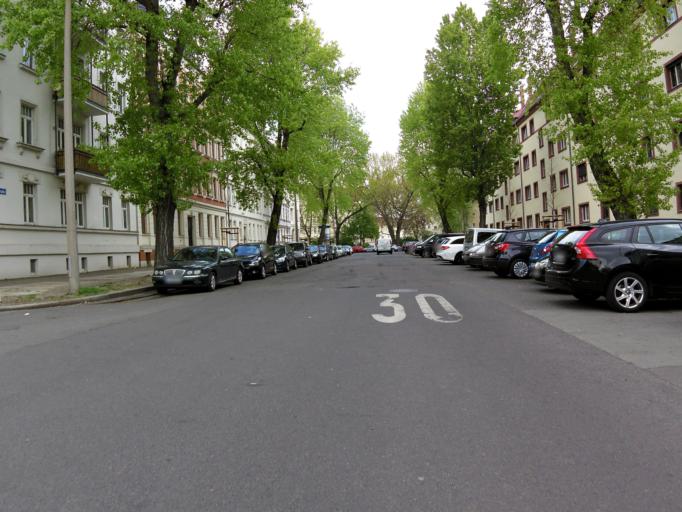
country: DE
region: Saxony
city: Leipzig
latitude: 51.3621
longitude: 12.3897
